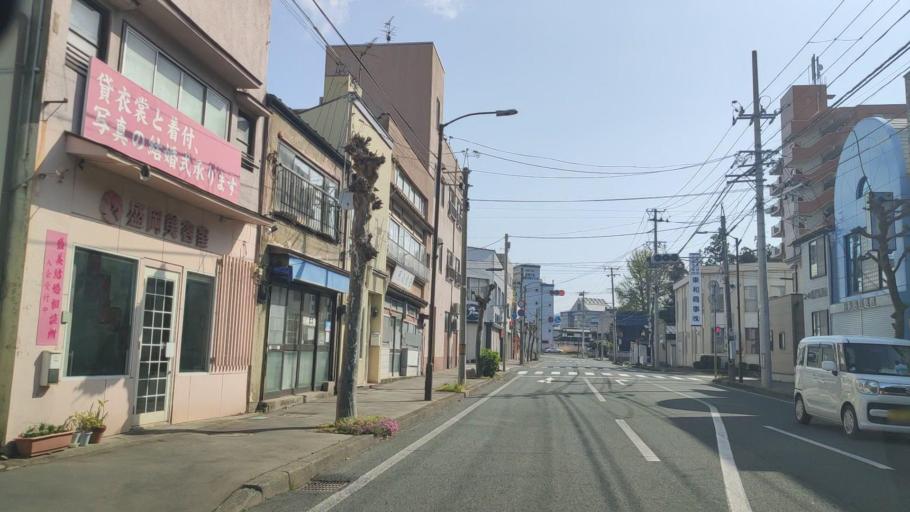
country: JP
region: Iwate
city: Morioka-shi
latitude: 39.6948
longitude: 141.1549
